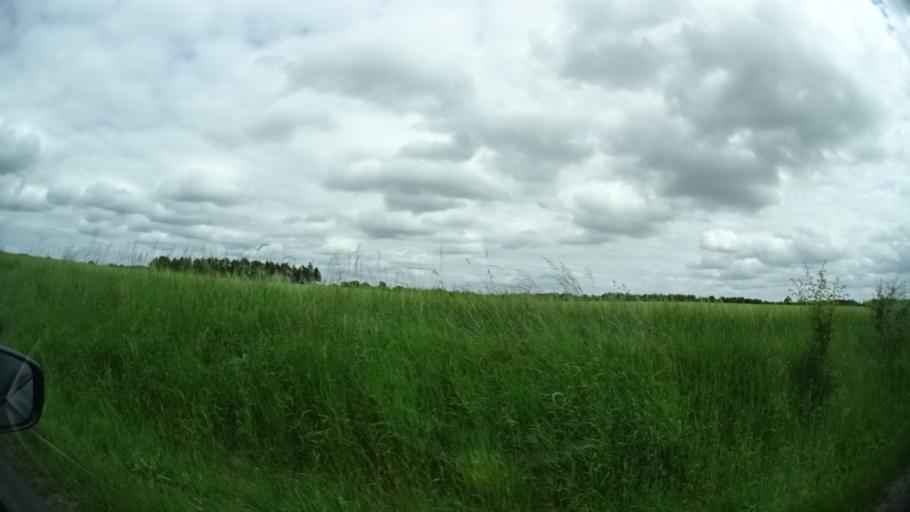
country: DK
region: Central Jutland
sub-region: Norddjurs Kommune
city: Grenaa
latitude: 56.4493
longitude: 10.7116
